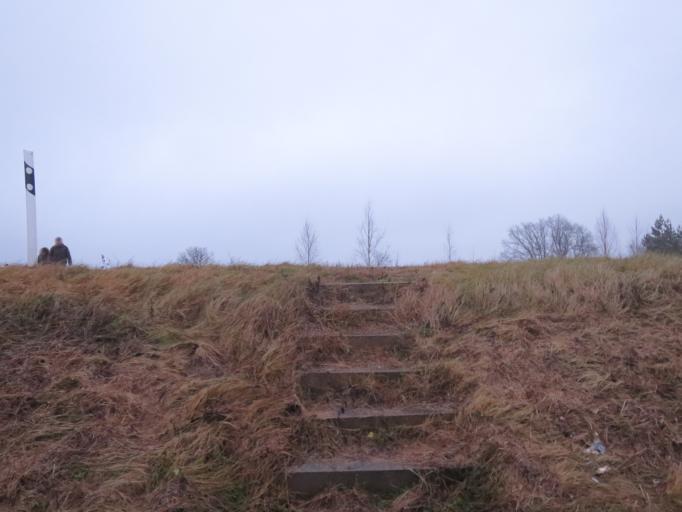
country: LV
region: Koknese
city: Koknese
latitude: 56.8803
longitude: 25.2943
